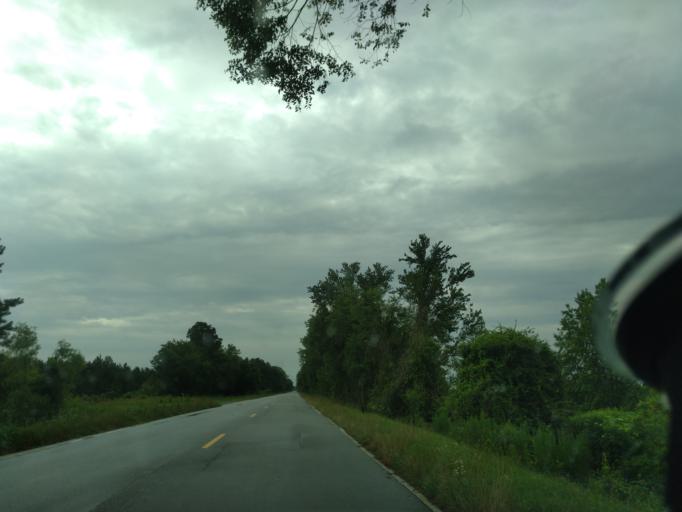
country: US
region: North Carolina
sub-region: Washington County
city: Plymouth
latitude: 35.8415
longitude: -76.5472
